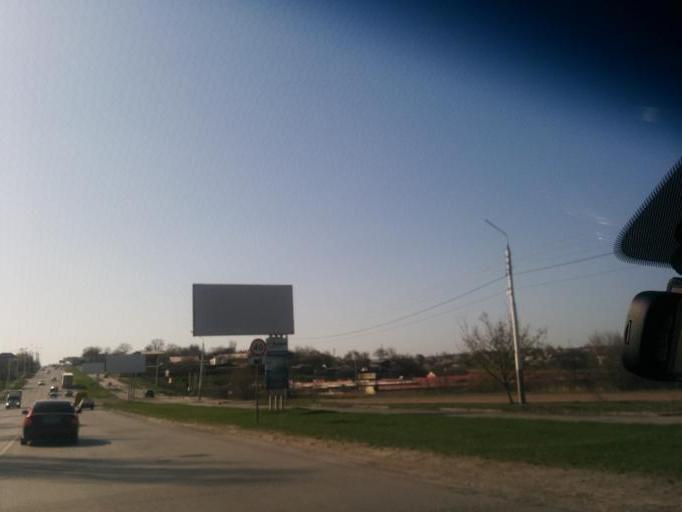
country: RU
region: Rostov
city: Shakhty
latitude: 47.7096
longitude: 40.1801
